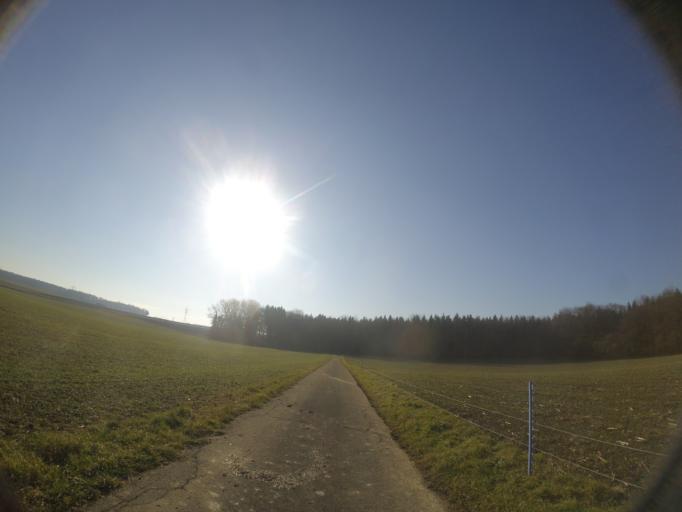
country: DE
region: Baden-Wuerttemberg
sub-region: Tuebingen Region
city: Beimerstetten
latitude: 48.4774
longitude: 9.9682
